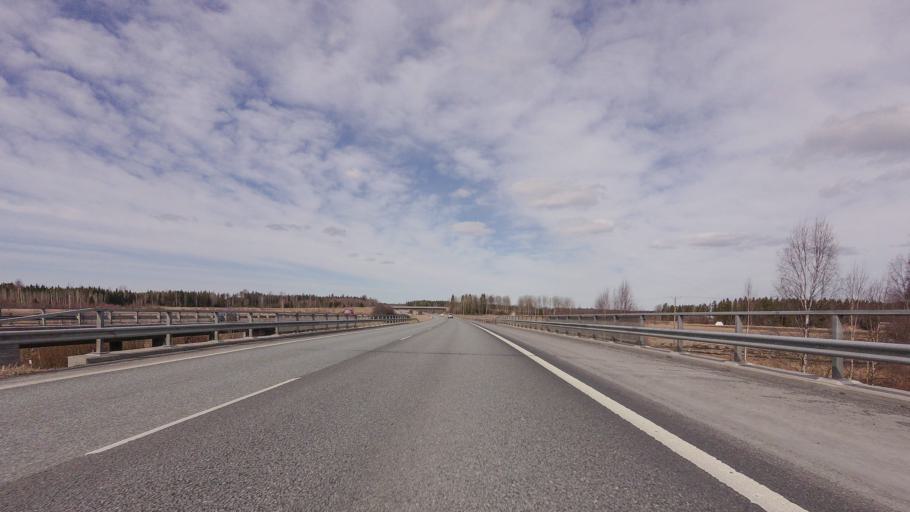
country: FI
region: Pirkanmaa
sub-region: Tampere
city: Lempaeaelae
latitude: 61.3108
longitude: 23.8228
